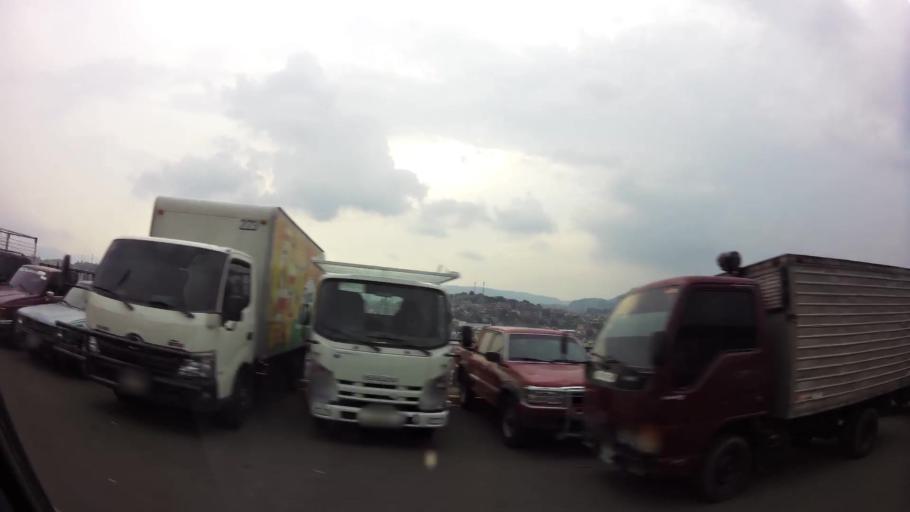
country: HN
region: Francisco Morazan
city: Tegucigalpa
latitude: 14.0954
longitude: -87.2047
